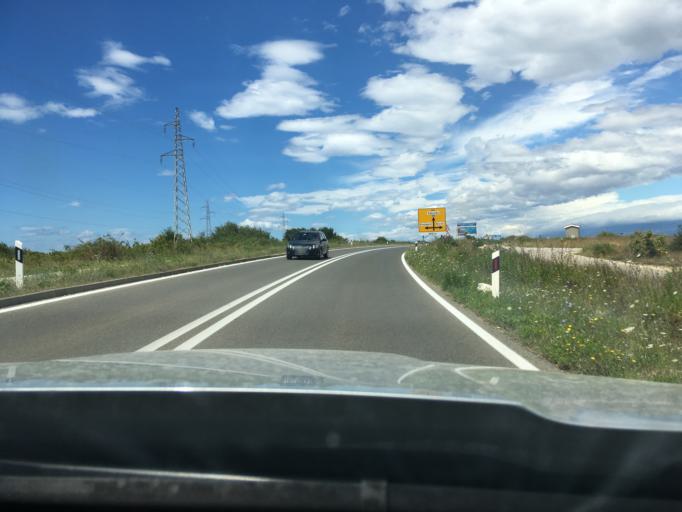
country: HR
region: Zadarska
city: Nin
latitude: 44.2415
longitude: 15.1689
